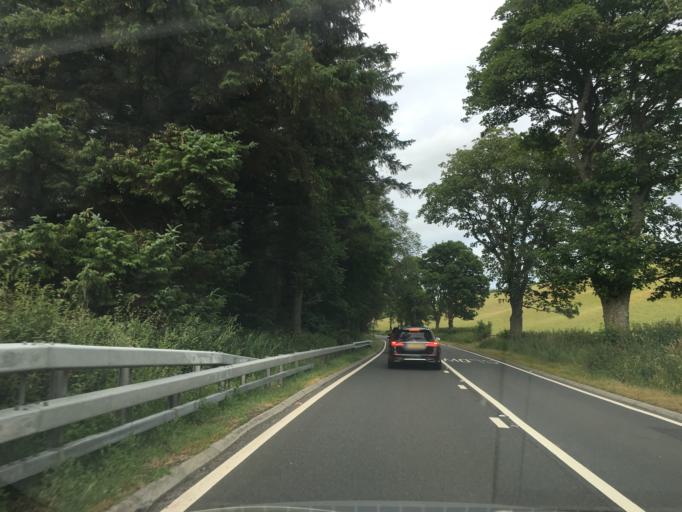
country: GB
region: Scotland
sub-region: South Lanarkshire
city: Biggar
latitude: 55.5523
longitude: -3.6367
